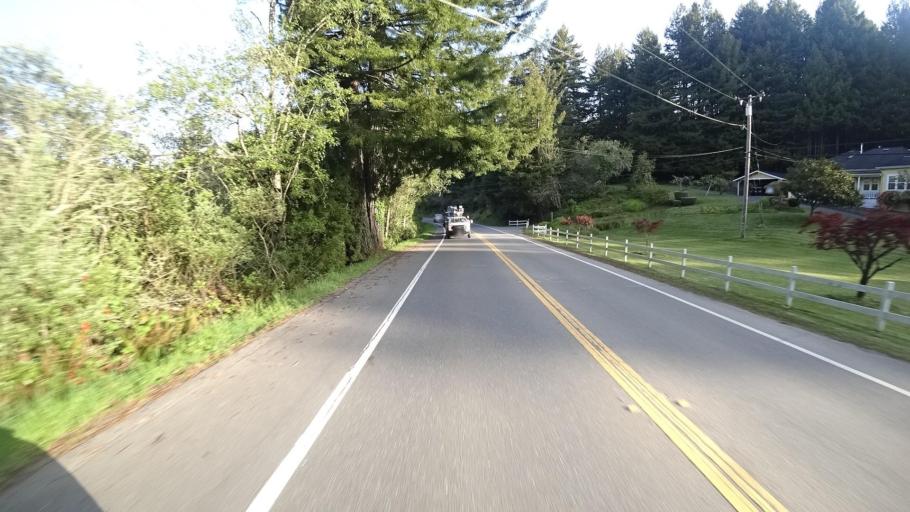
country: US
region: California
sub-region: Humboldt County
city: Myrtletown
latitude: 40.7628
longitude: -124.0631
